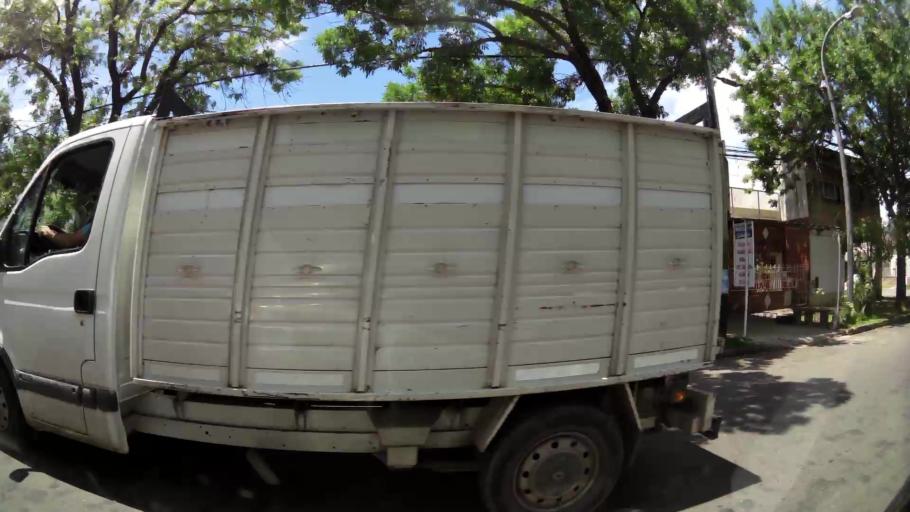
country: AR
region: Santa Fe
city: Gobernador Galvez
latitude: -33.0012
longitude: -60.6295
